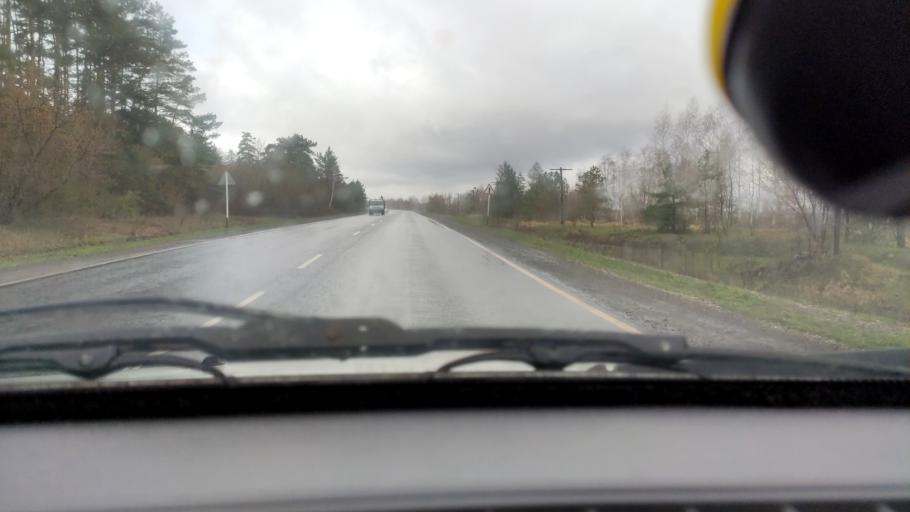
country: RU
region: Samara
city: Povolzhskiy
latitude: 53.6030
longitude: 49.5998
